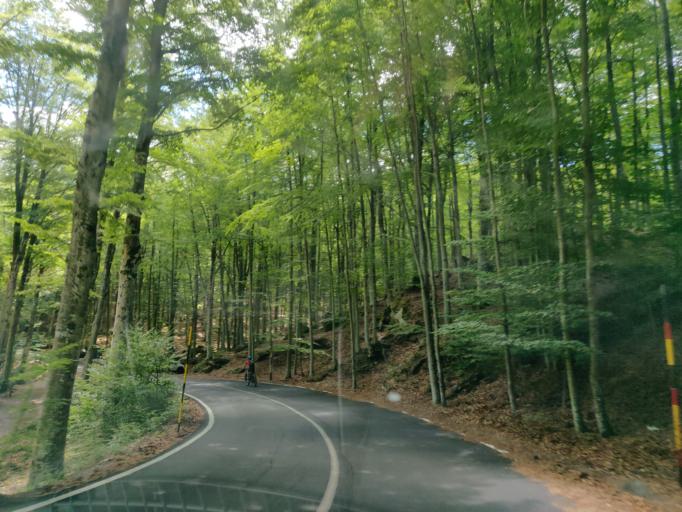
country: IT
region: Tuscany
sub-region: Provincia di Siena
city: Abbadia San Salvatore
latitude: 42.9008
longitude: 11.6380
